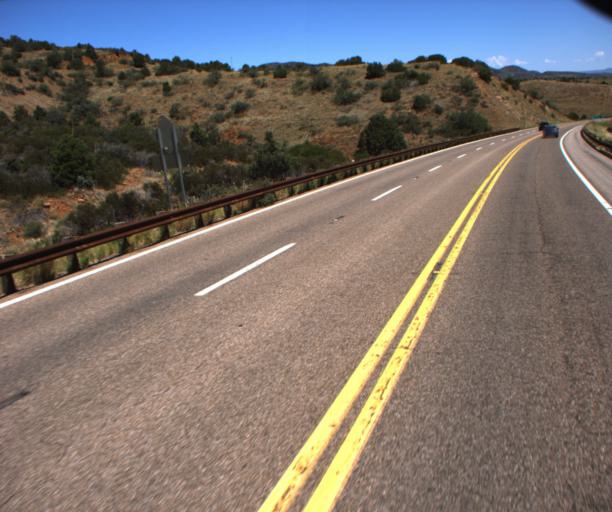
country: US
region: Arizona
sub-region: Gila County
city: Globe
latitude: 33.5176
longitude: -110.7012
